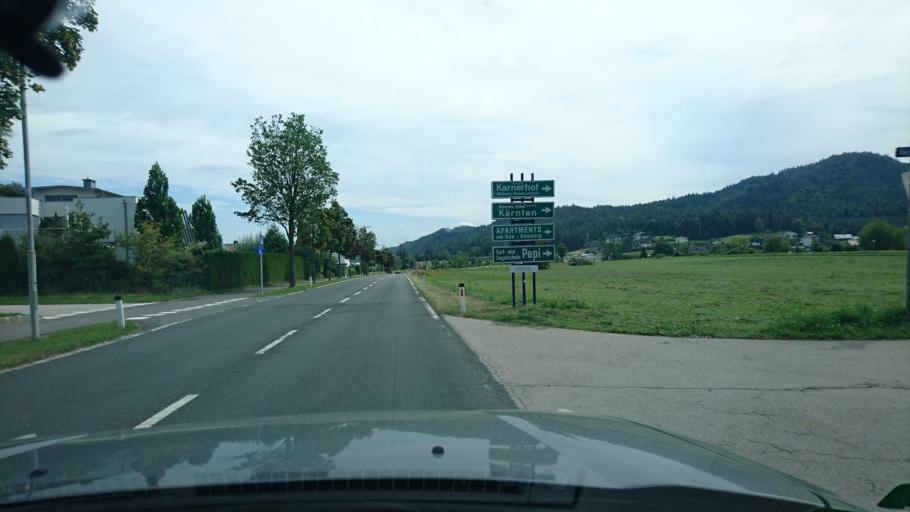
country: AT
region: Carinthia
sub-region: Politischer Bezirk Villach Land
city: Wernberg
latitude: 46.5895
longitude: 13.9273
